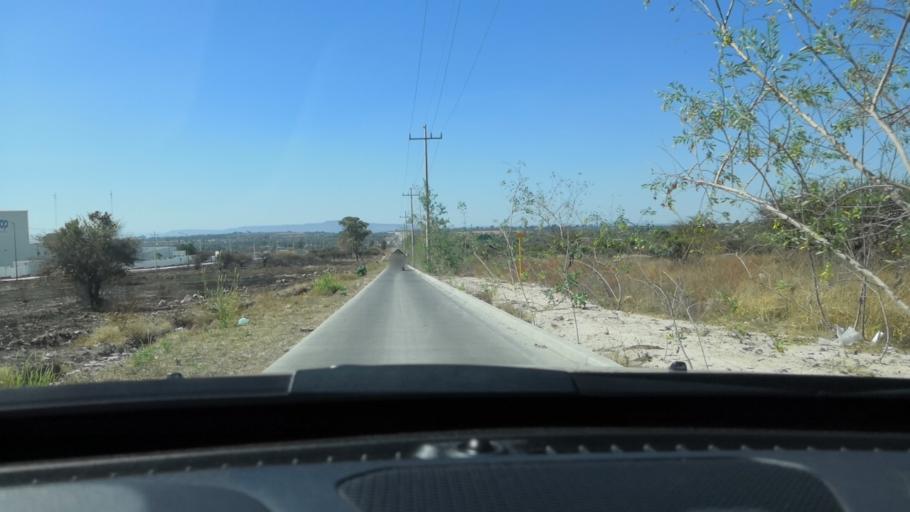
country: MX
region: Guanajuato
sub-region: Leon
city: Centro Familiar la Soledad
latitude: 21.1072
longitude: -101.7643
